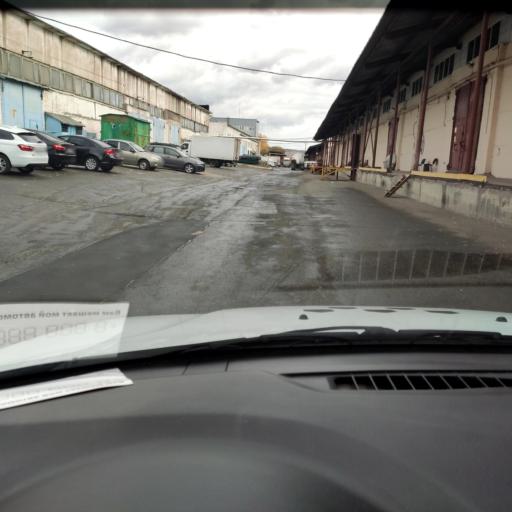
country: RU
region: Samara
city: Zhigulevsk
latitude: 53.4834
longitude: 49.4876
